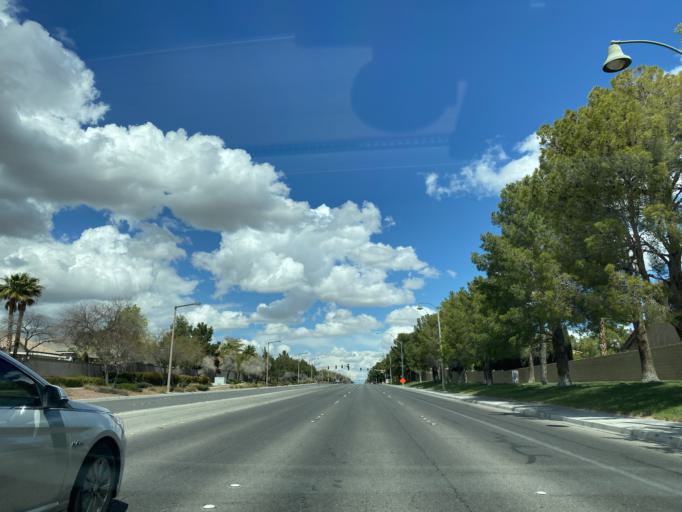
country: US
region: Nevada
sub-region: Clark County
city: Summerlin South
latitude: 36.1348
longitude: -115.3152
